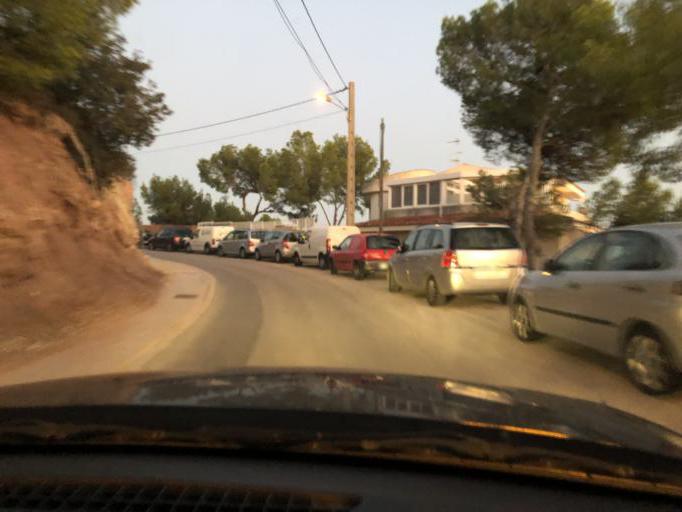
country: ES
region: Balearic Islands
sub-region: Illes Balears
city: Santa Ponsa
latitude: 39.5206
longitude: 2.4822
